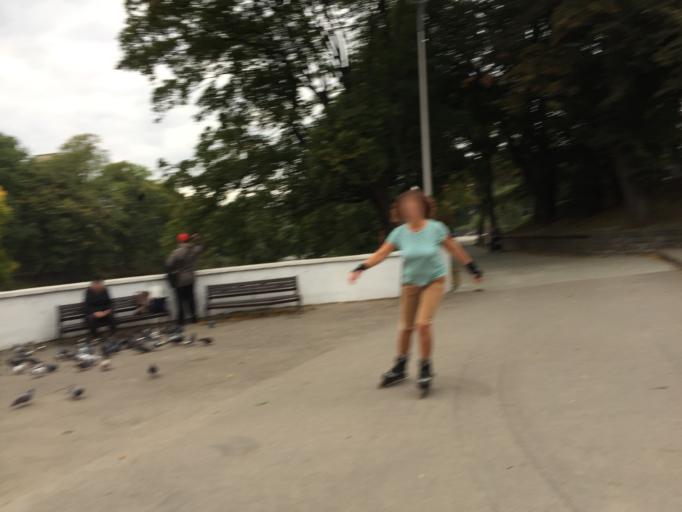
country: RU
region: Kaliningrad
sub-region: Gorod Kaliningrad
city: Kaliningrad
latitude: 54.7146
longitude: 20.5179
